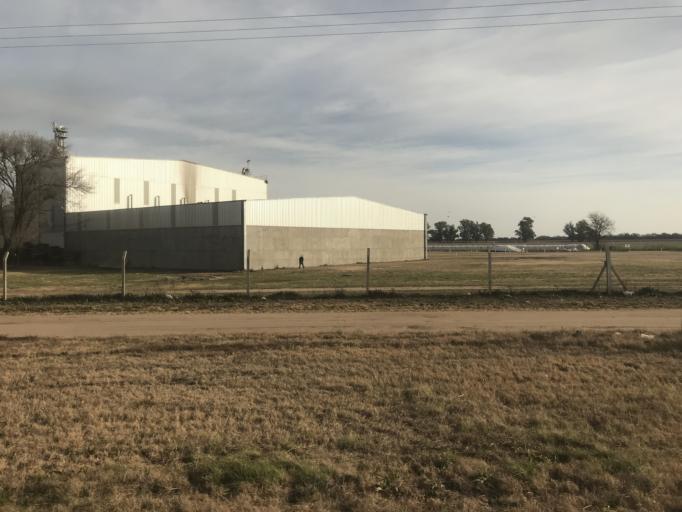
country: AR
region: Cordoba
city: Pilar
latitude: -31.6717
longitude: -63.8949
